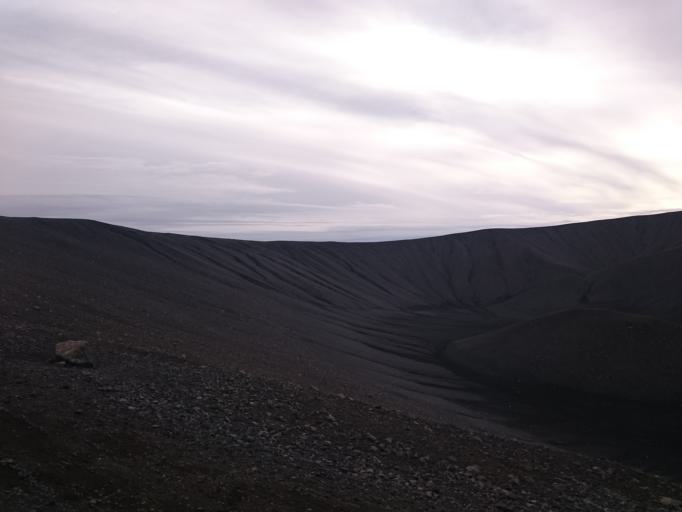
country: IS
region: Northeast
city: Laugar
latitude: 65.6087
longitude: -16.8775
